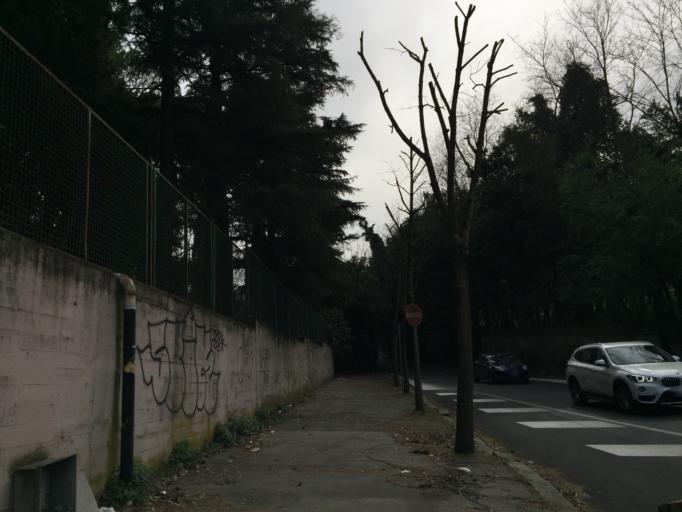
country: VA
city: Vatican City
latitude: 41.8909
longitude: 12.4585
